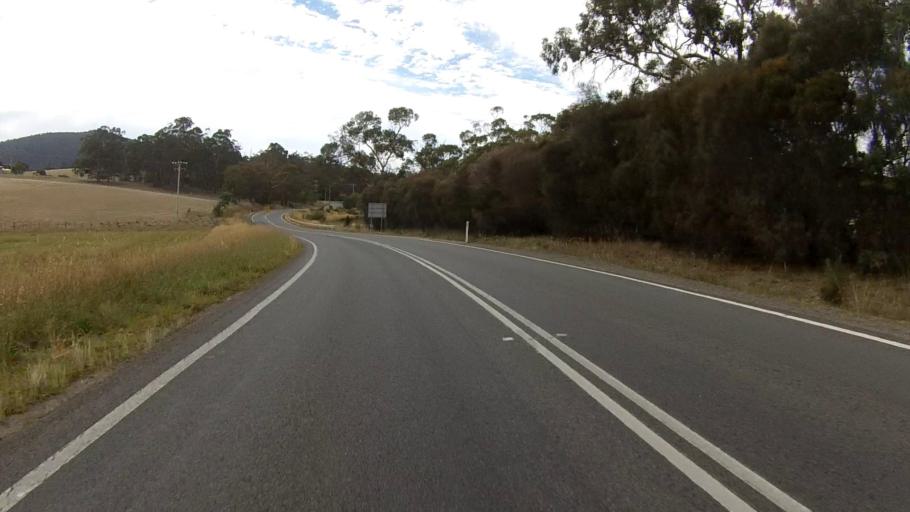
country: AU
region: Tasmania
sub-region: Sorell
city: Sorell
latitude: -42.7077
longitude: 147.5036
